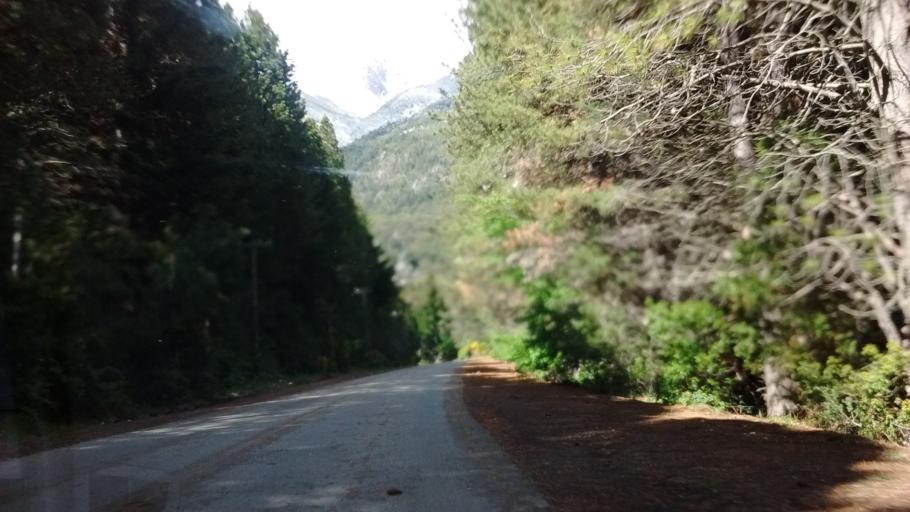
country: AR
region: Rio Negro
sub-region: Departamento de Bariloche
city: San Carlos de Bariloche
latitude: -41.0752
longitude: -71.5451
